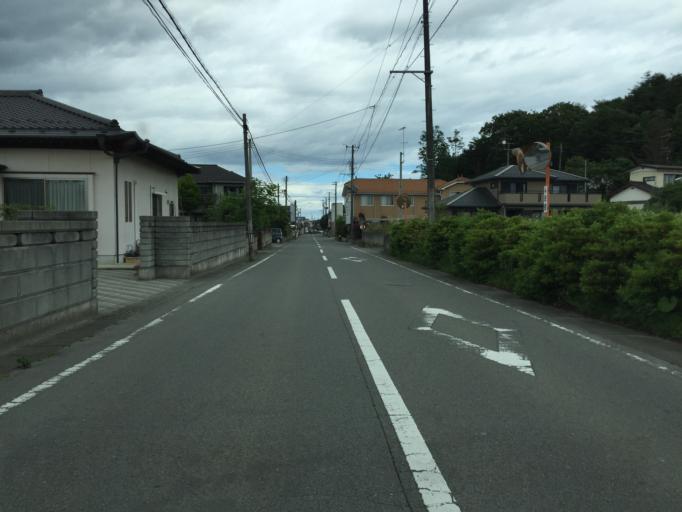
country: JP
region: Fukushima
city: Namie
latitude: 37.6266
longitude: 140.9618
